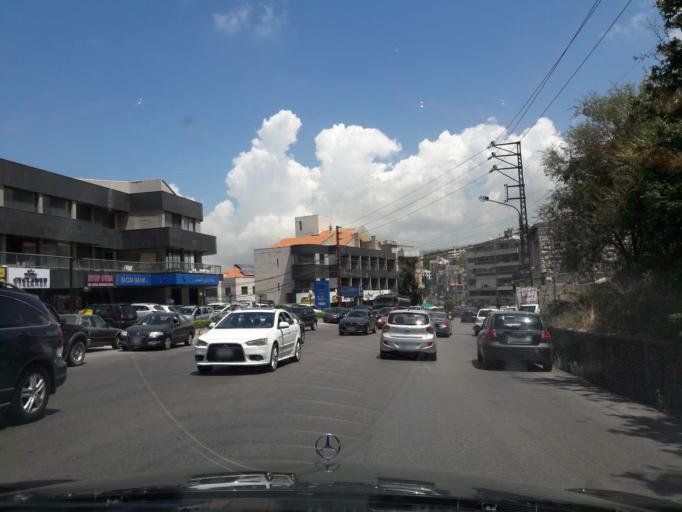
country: LB
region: Mont-Liban
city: Djounie
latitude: 33.9253
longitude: 35.6358
